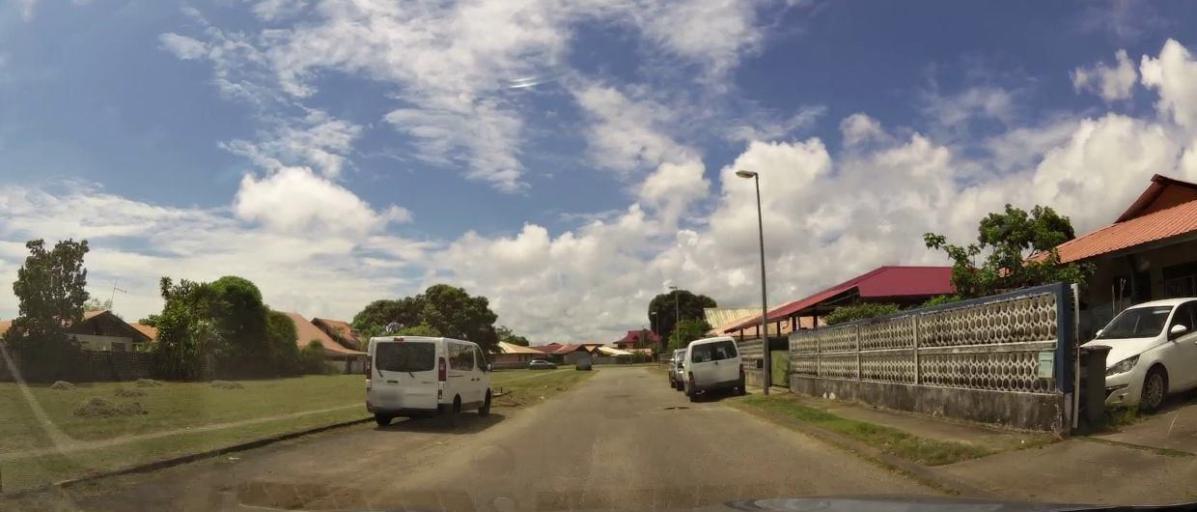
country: GF
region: Guyane
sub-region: Guyane
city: Kourou
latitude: 5.1679
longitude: -52.6547
